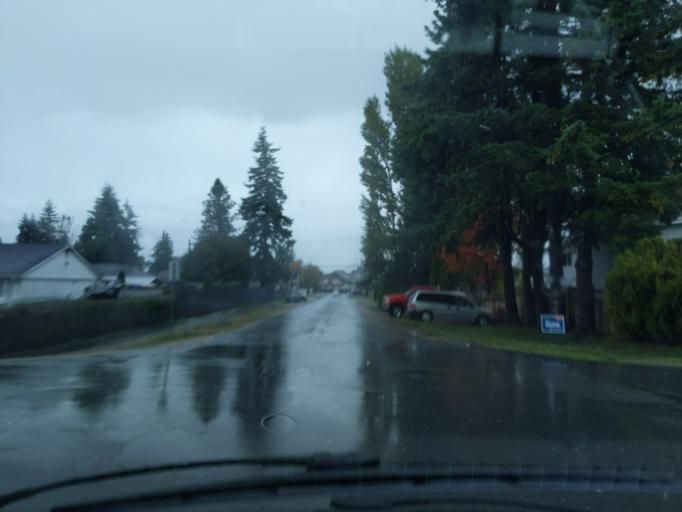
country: CA
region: British Columbia
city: New Westminster
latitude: 49.1969
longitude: -122.8624
